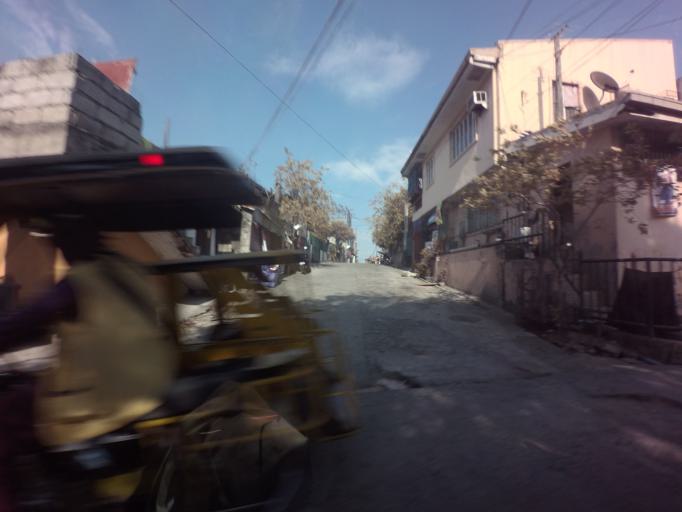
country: PH
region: Calabarzon
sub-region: Province of Rizal
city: Taguig
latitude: 14.4978
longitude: 121.0591
